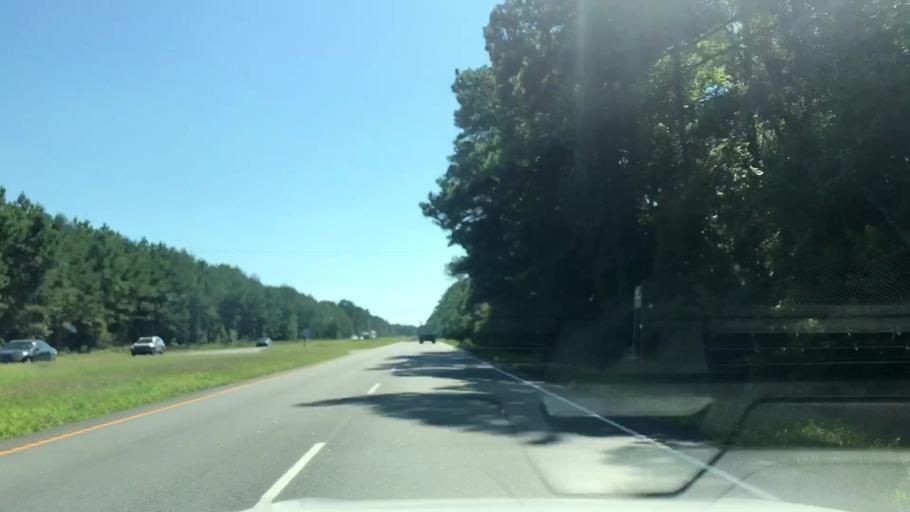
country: US
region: South Carolina
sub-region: Charleston County
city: Awendaw
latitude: 33.0881
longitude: -79.4881
